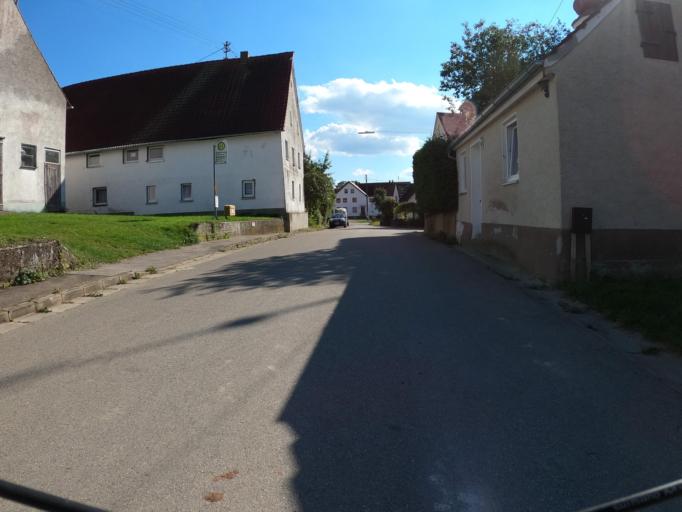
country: DE
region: Bavaria
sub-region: Swabia
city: Roggenburg
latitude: 48.3147
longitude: 10.2439
